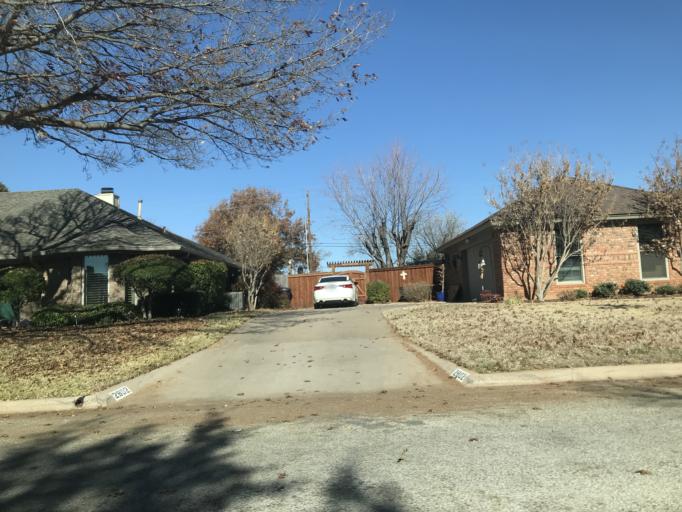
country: US
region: Texas
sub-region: Taylor County
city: Abilene
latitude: 32.3835
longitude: -99.7596
